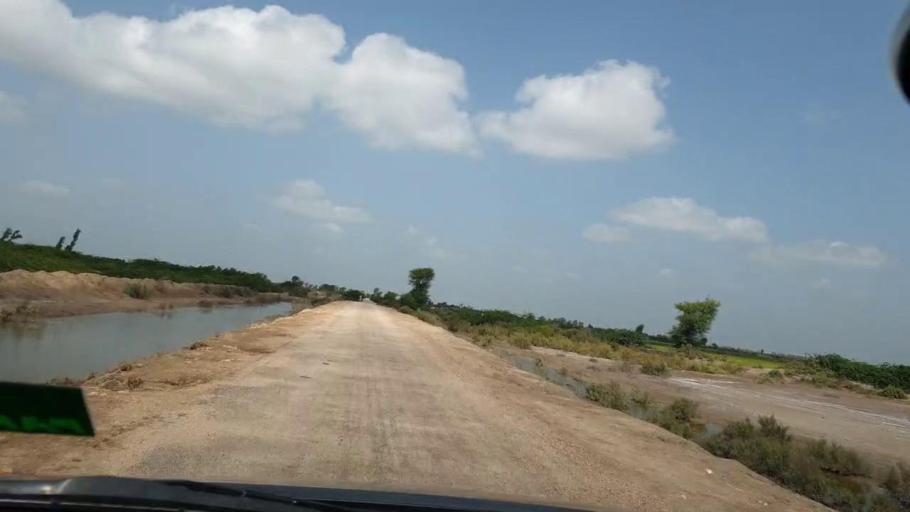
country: PK
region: Sindh
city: Kadhan
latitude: 24.6006
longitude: 69.1240
